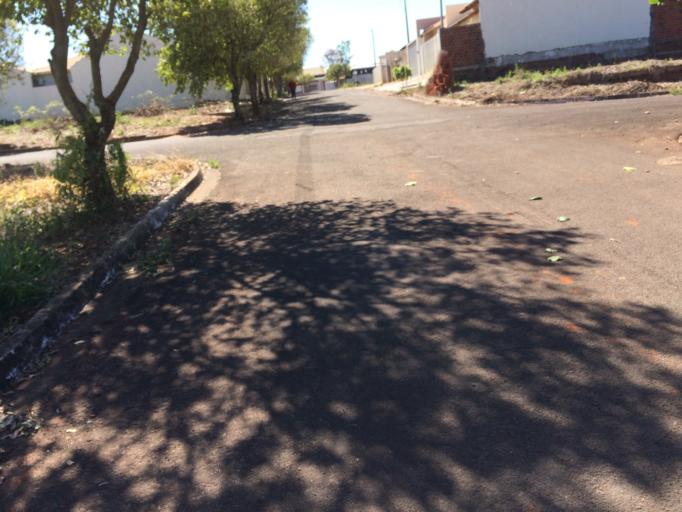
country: BR
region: Parana
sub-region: Cianorte
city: Cianorte
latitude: -23.5405
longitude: -52.5942
